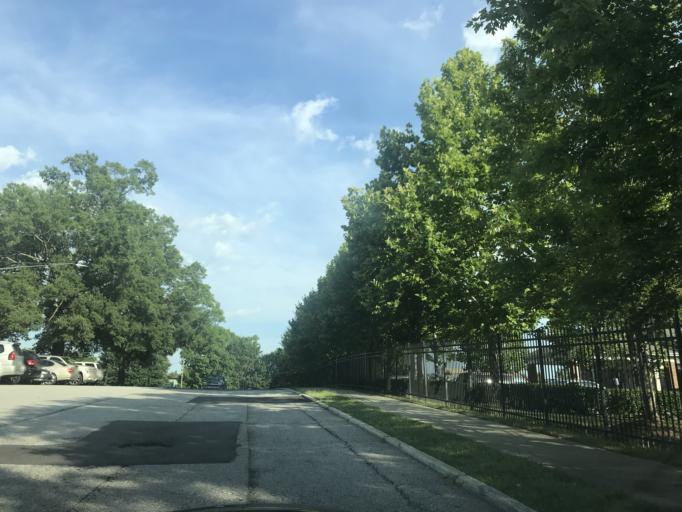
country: US
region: North Carolina
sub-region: Wake County
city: Raleigh
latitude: 35.7720
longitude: -78.6277
